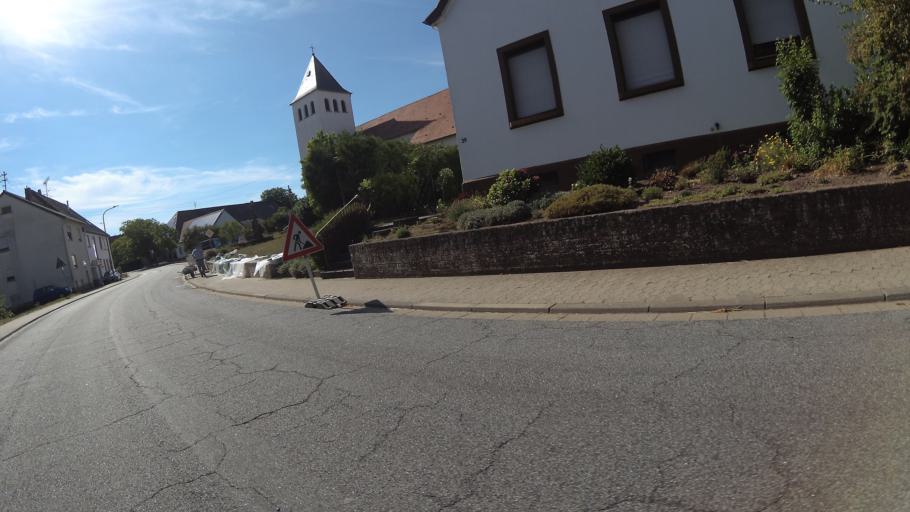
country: DE
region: Saarland
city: Blieskastel
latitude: 49.1680
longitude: 7.2888
